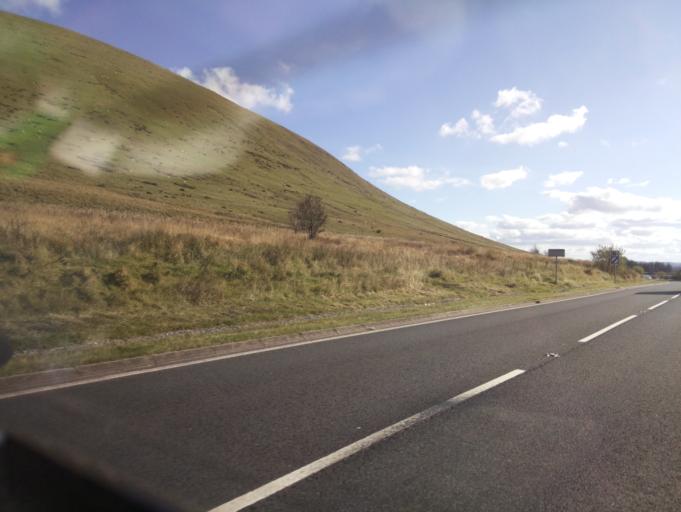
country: GB
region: Wales
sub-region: Sir Powys
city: Brecon
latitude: 51.8614
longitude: -3.4712
